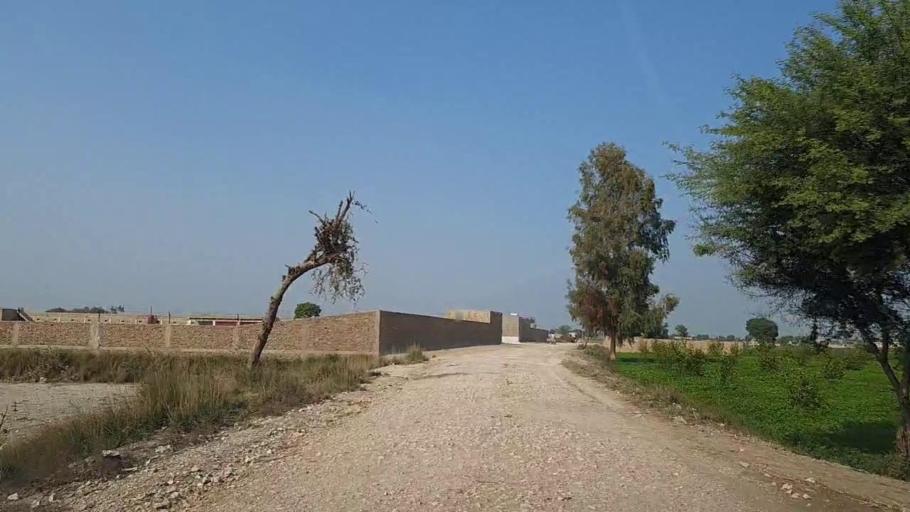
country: PK
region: Sindh
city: Moro
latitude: 26.6886
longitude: 67.9482
